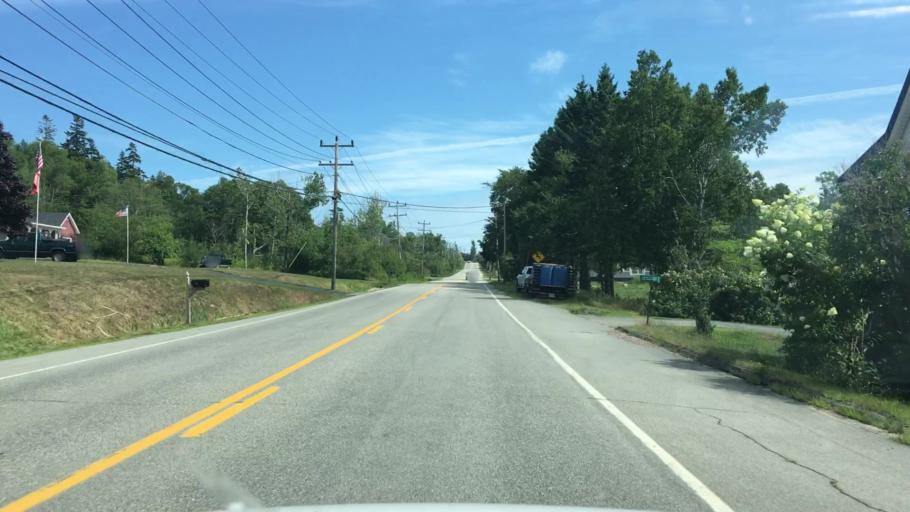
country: US
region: Maine
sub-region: Washington County
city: Eastport
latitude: 44.9188
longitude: -67.0142
